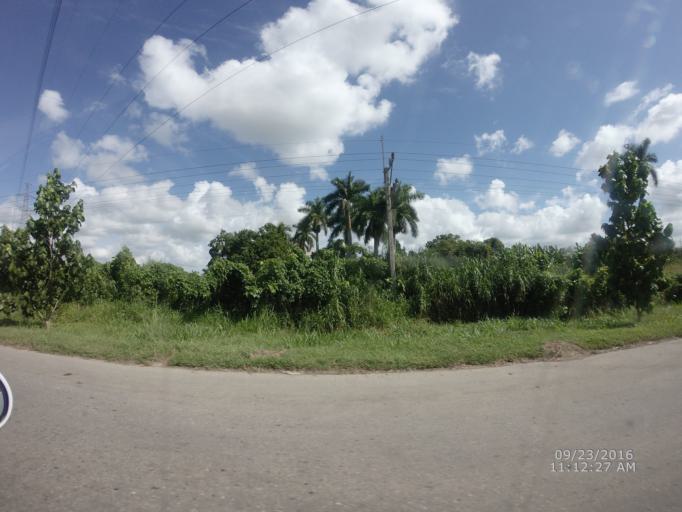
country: CU
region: La Habana
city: Arroyo Naranjo
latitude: 23.0296
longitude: -82.2840
